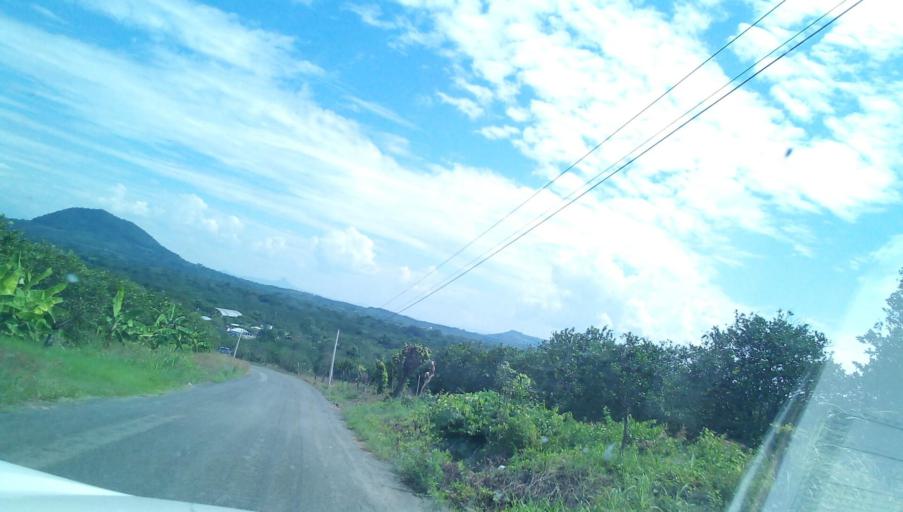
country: MX
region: Veracruz
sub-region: Alamo Temapache
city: Vegas de la Soledad y Soledad Dos
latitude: 20.8990
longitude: -97.9438
